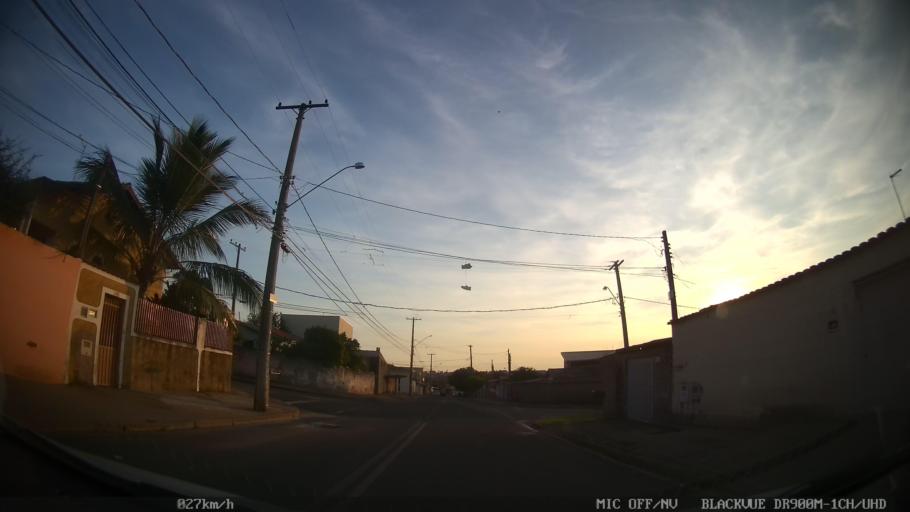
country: BR
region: Sao Paulo
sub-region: Campinas
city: Campinas
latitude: -22.9762
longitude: -47.1344
